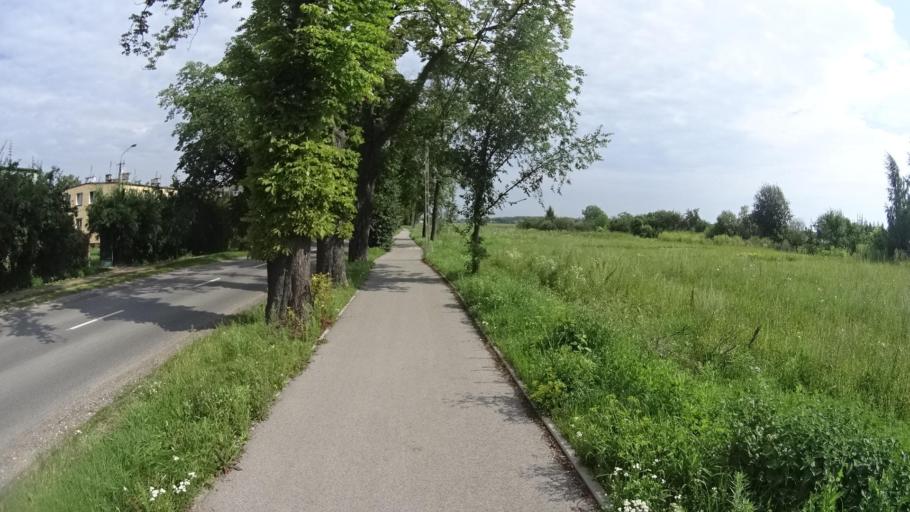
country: PL
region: Masovian Voivodeship
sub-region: Powiat pruszkowski
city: Nadarzyn
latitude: 52.0513
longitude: 20.7834
